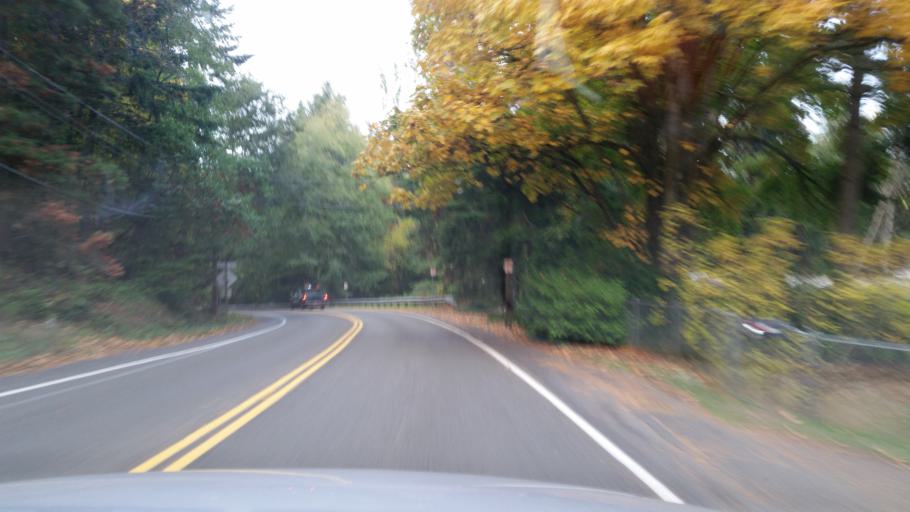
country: US
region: Washington
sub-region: King County
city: Shoreline
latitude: 47.7483
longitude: -122.3556
